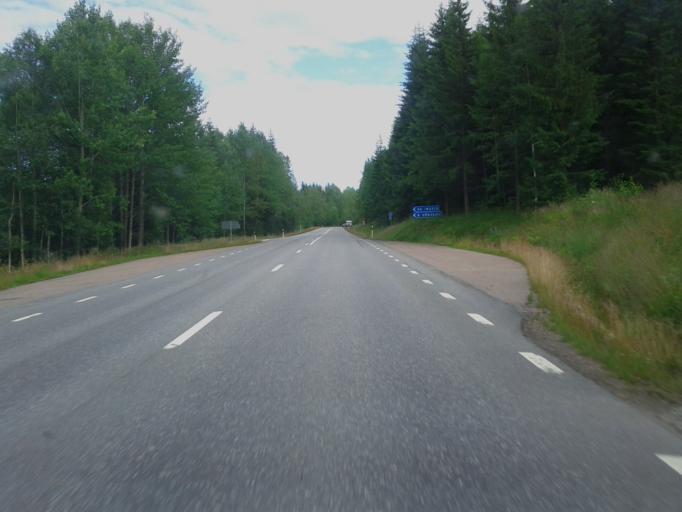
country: SE
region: Dalarna
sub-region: Faluns Kommun
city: Bjursas
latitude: 60.7405
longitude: 15.4200
